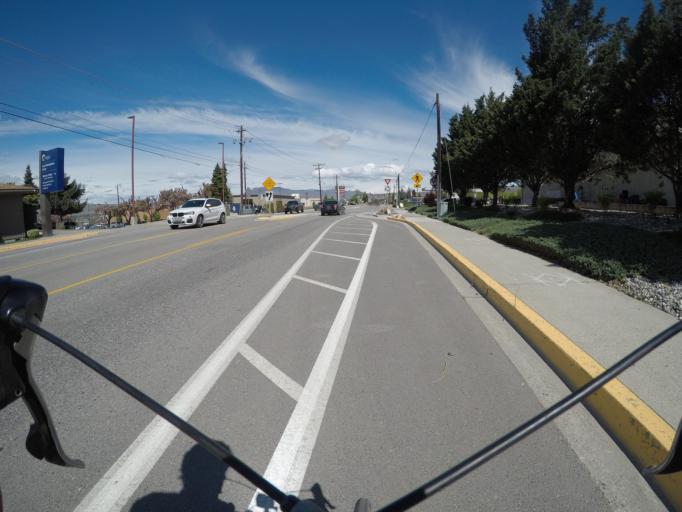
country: US
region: Washington
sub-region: Douglas County
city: East Wenatchee
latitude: 47.4044
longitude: -120.2818
